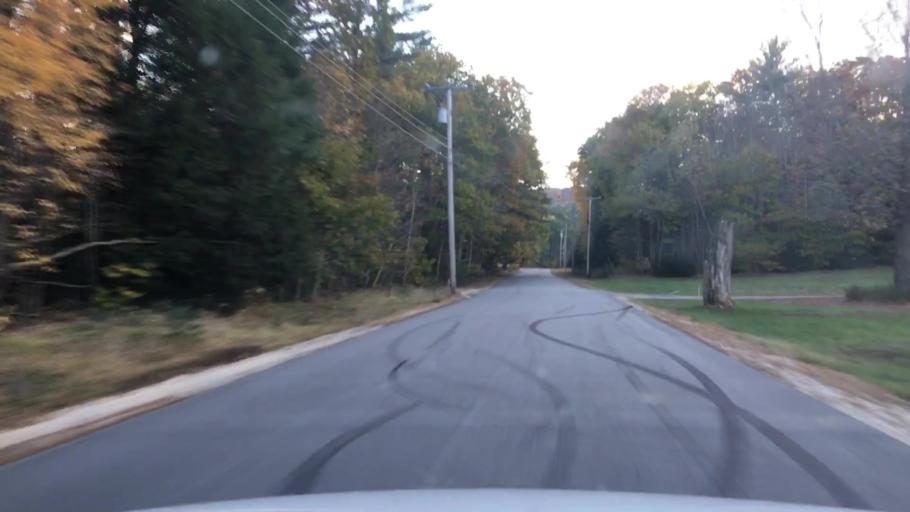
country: US
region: Maine
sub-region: Cumberland County
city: Harrison
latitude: 44.2386
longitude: -70.7450
